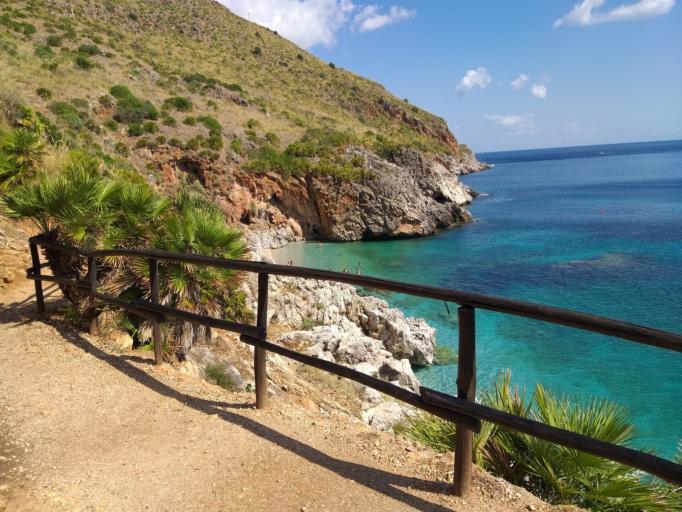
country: IT
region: Sicily
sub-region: Trapani
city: Castelluzzo
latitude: 38.0872
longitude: 12.8052
